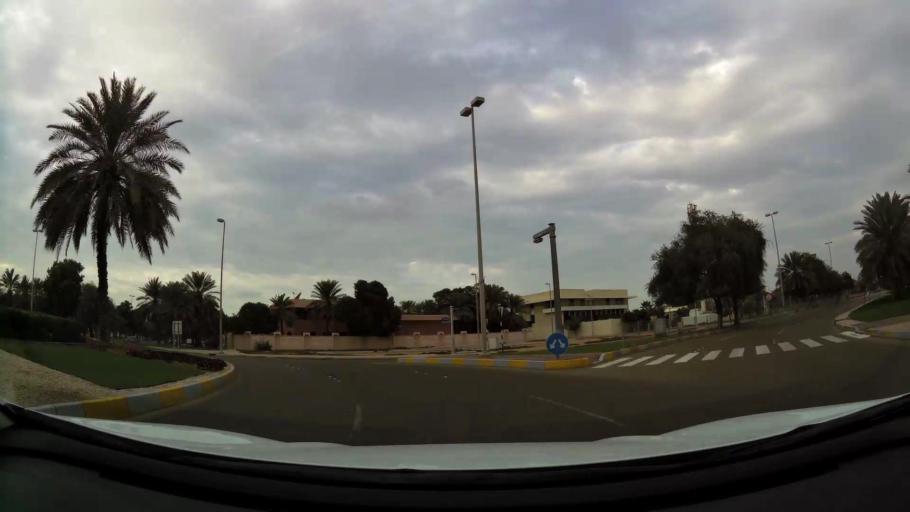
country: AE
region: Abu Dhabi
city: Abu Dhabi
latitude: 24.4410
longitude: 54.3614
